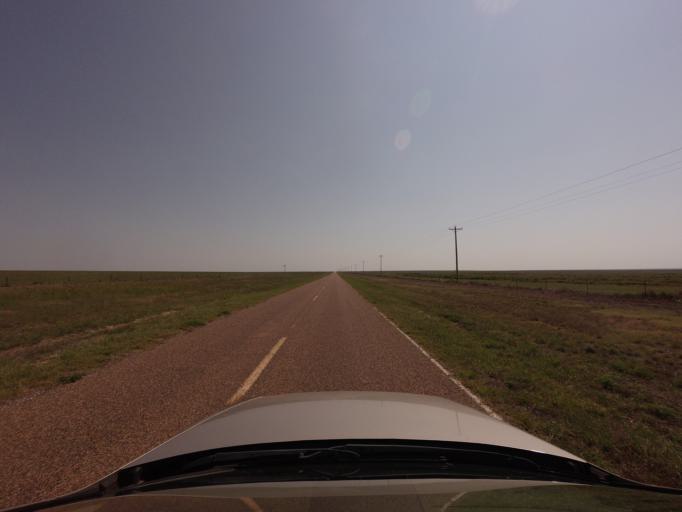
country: US
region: New Mexico
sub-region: Curry County
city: Cannon Air Force Base
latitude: 34.6330
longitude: -103.3862
